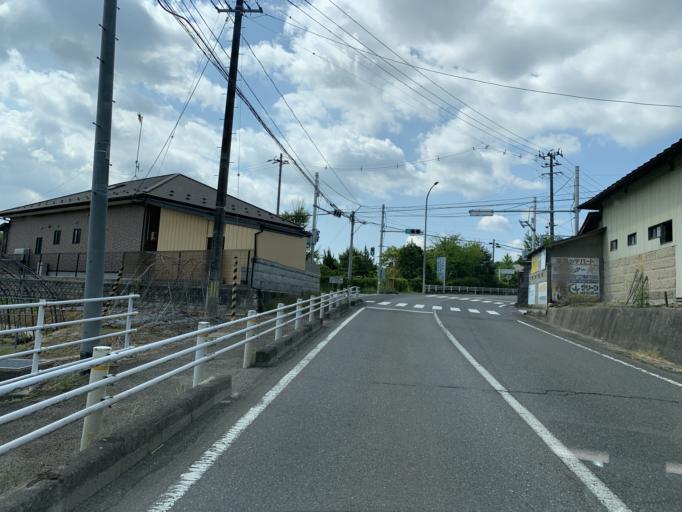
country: JP
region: Miyagi
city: Furukawa
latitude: 38.7677
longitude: 140.9631
